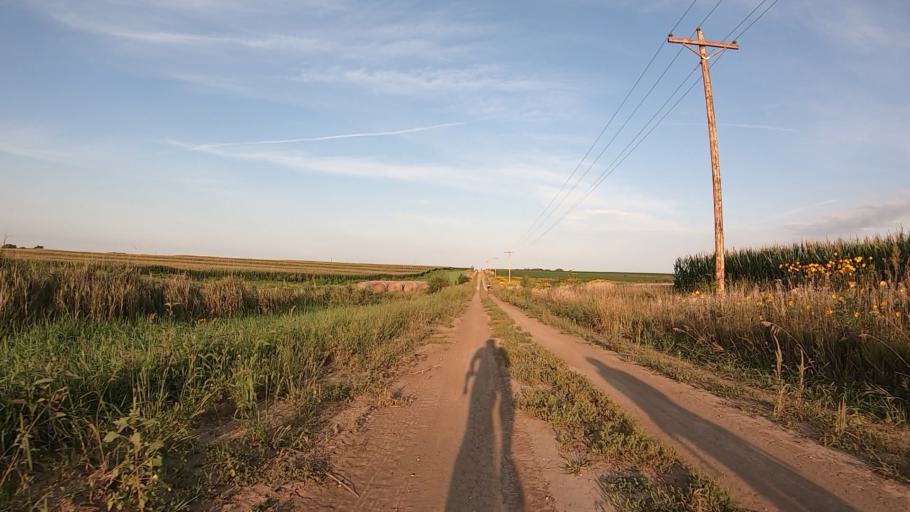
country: US
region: Kansas
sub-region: Marshall County
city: Marysville
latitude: 39.7694
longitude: -96.7273
